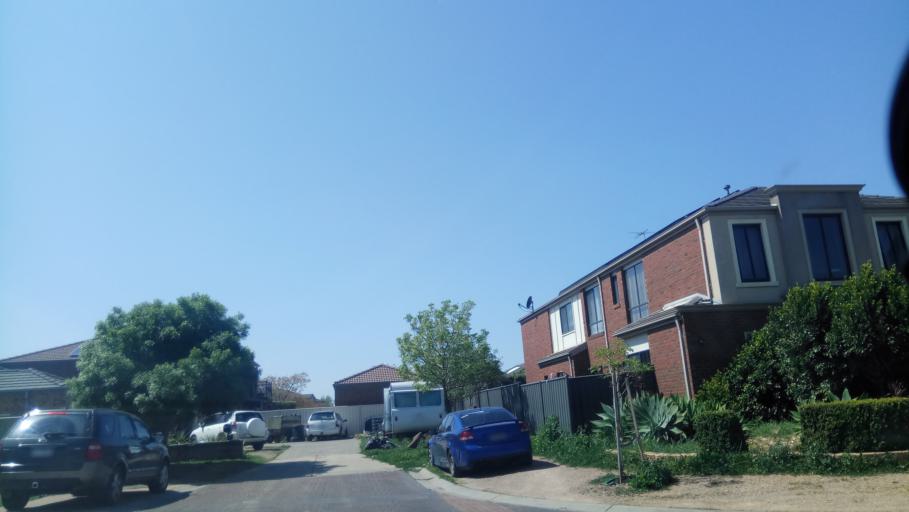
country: AU
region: Victoria
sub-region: Wyndham
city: Point Cook
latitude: -37.8936
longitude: 144.7418
